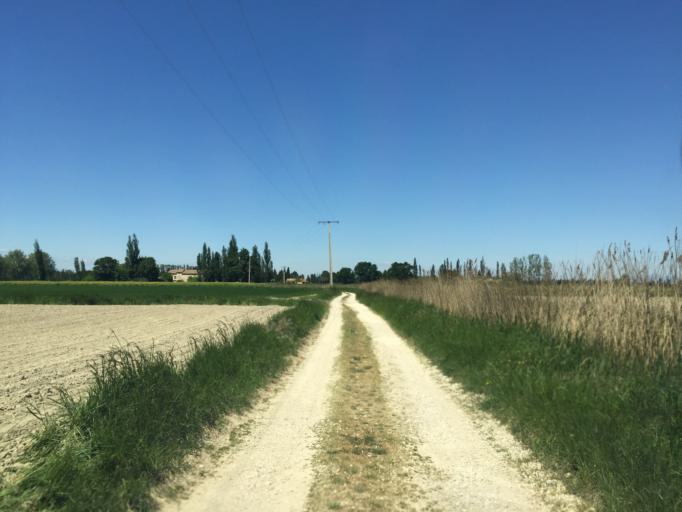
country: FR
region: Provence-Alpes-Cote d'Azur
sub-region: Departement du Vaucluse
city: Bedarrides
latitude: 44.0618
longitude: 4.9029
